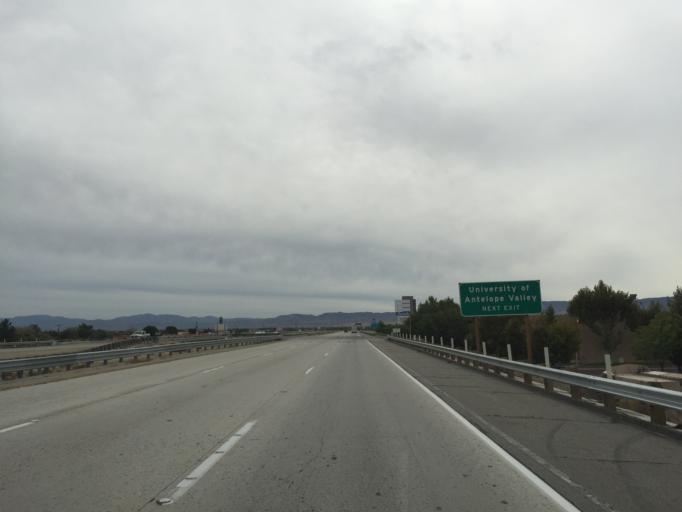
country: US
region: California
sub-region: Los Angeles County
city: Lancaster
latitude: 34.6977
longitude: -118.1703
